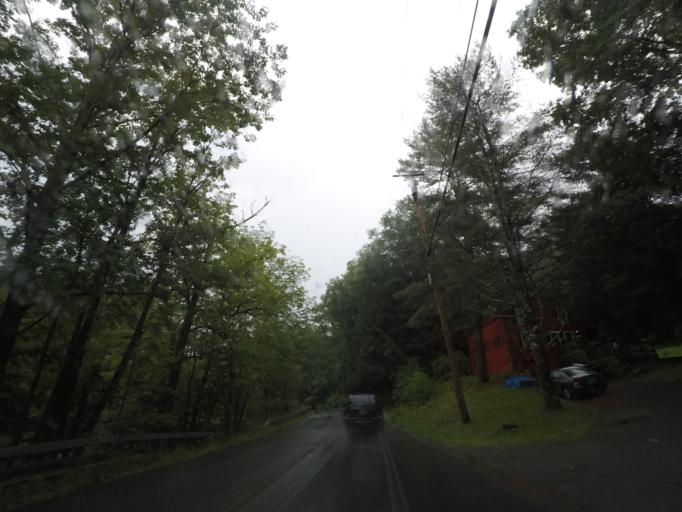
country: US
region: New York
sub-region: Rensselaer County
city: Poestenkill
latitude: 42.6770
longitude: -73.5370
